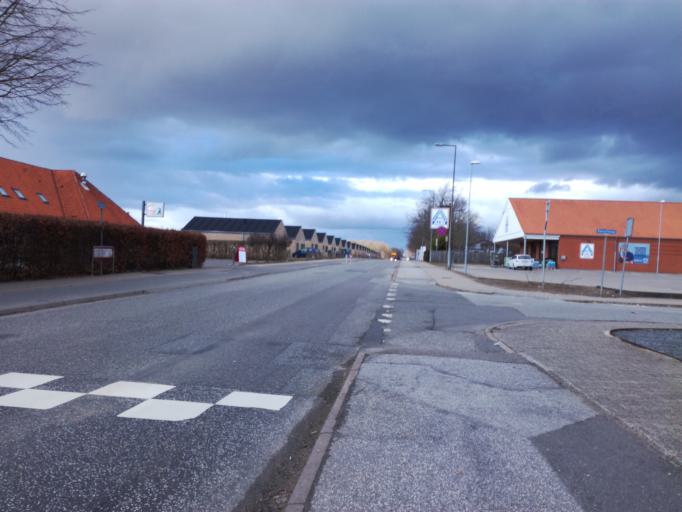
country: DK
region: South Denmark
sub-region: Fredericia Kommune
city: Fredericia
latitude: 55.5811
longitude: 9.7671
